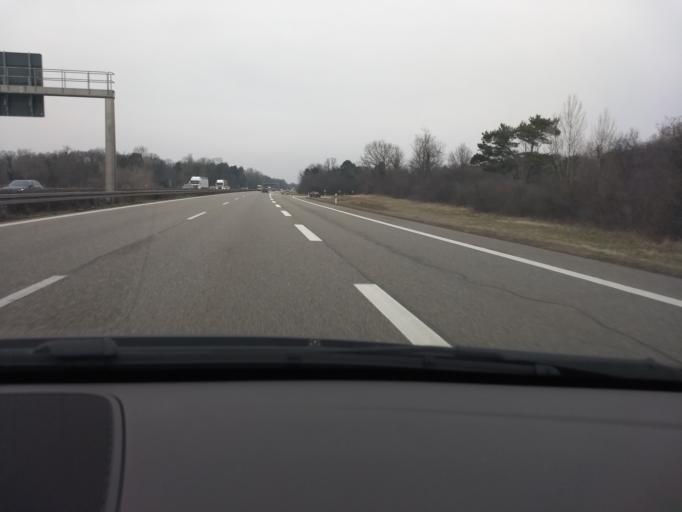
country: FR
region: Alsace
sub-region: Departement du Haut-Rhin
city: Ottmarsheim
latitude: 47.7795
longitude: 7.5359
